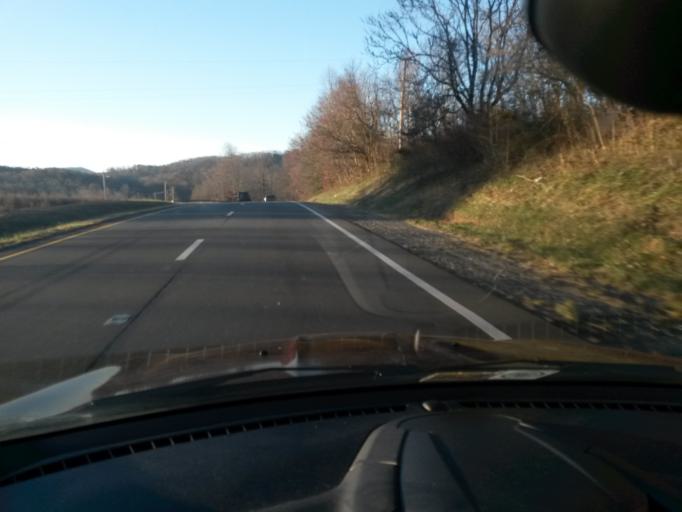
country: US
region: Virginia
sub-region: Franklin County
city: Henry Fork
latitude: 36.9100
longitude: -79.8659
